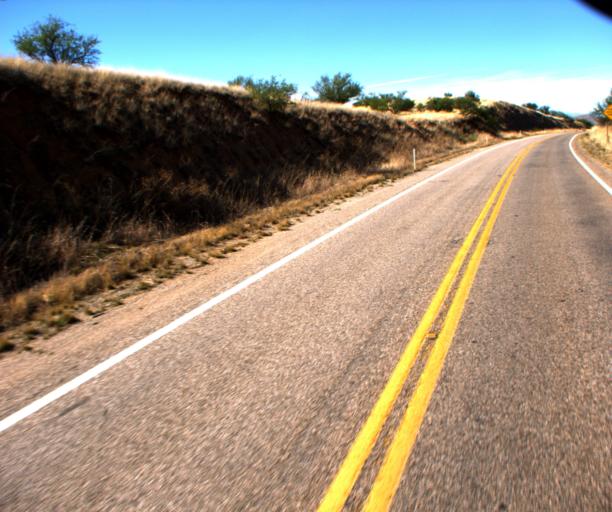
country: US
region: Arizona
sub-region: Pima County
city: Corona de Tucson
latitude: 31.8140
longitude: -110.7120
